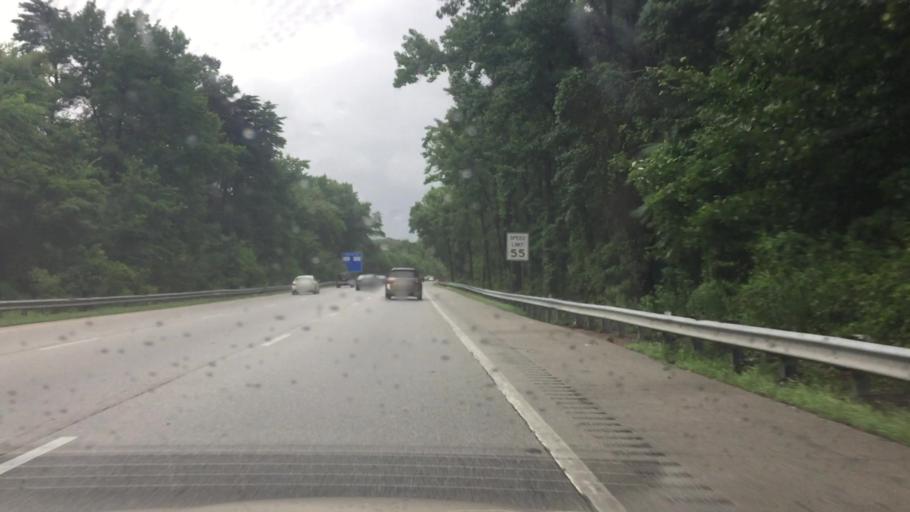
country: US
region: Maryland
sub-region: Anne Arundel County
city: Jessup
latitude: 39.1475
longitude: -76.7521
